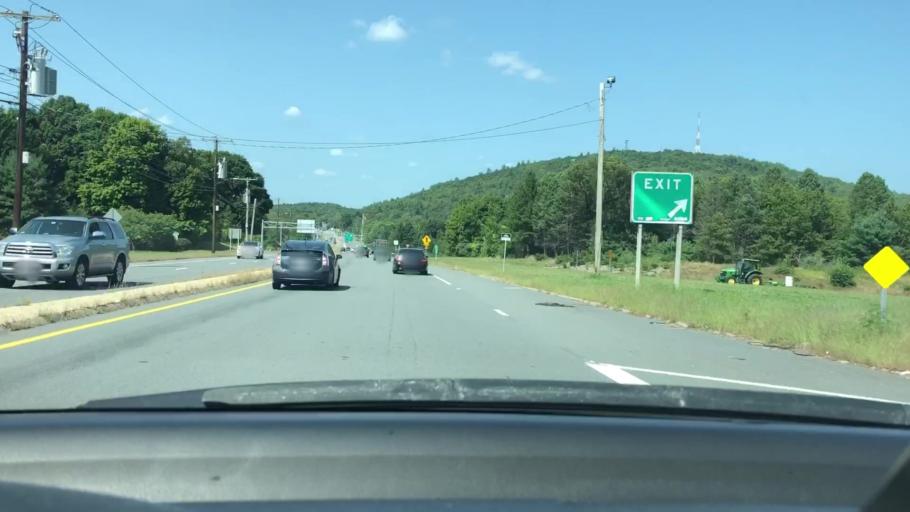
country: US
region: Massachusetts
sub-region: Norfolk County
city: Canton
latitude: 42.2006
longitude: -71.1189
